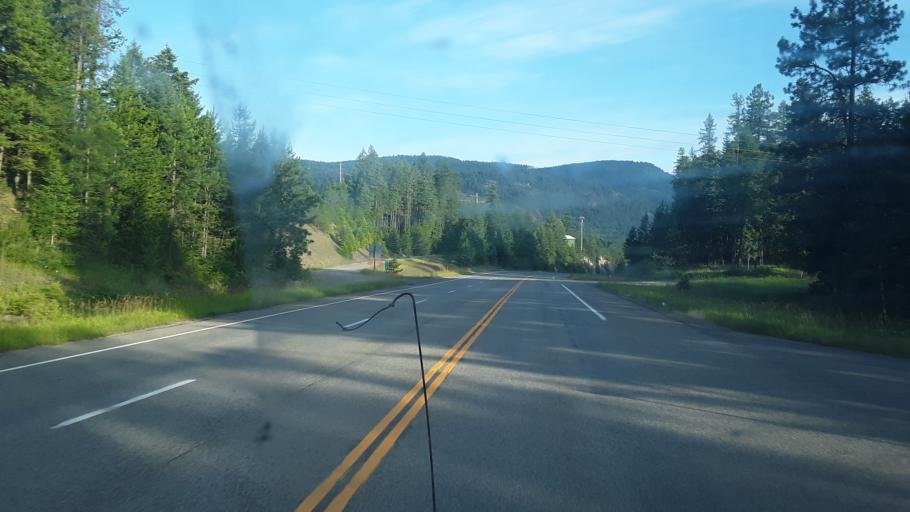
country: US
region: Montana
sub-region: Lincoln County
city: Libby
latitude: 48.4412
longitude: -115.8703
